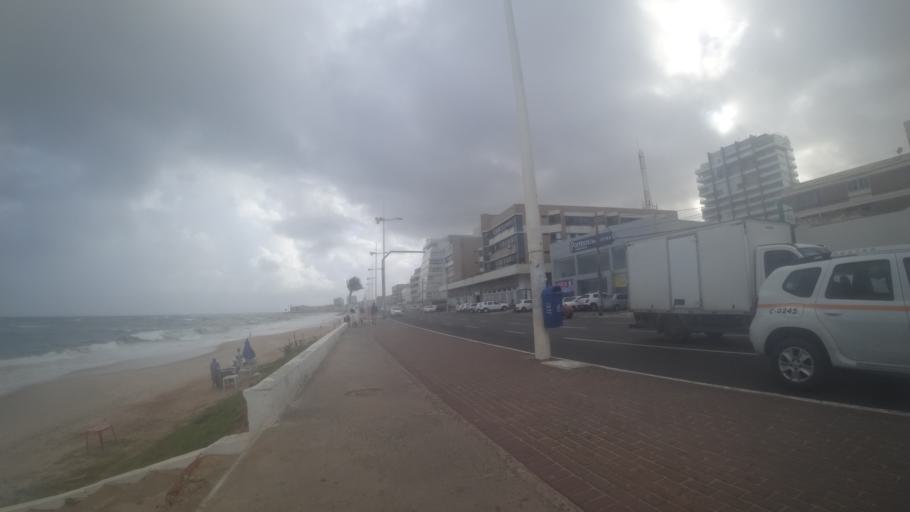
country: BR
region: Bahia
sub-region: Salvador
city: Salvador
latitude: -13.0087
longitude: -38.4613
